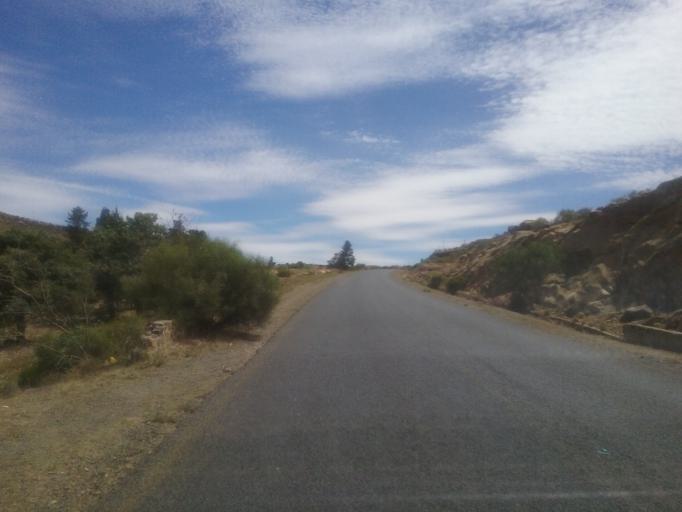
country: LS
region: Mohale's Hoek District
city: Mohale's Hoek
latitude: -30.0818
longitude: 27.4283
